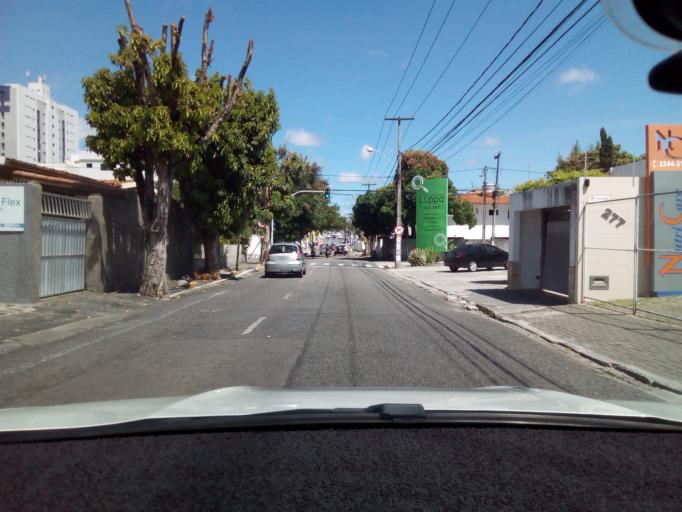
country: BR
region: Paraiba
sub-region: Joao Pessoa
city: Joao Pessoa
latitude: -7.1171
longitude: -34.8553
